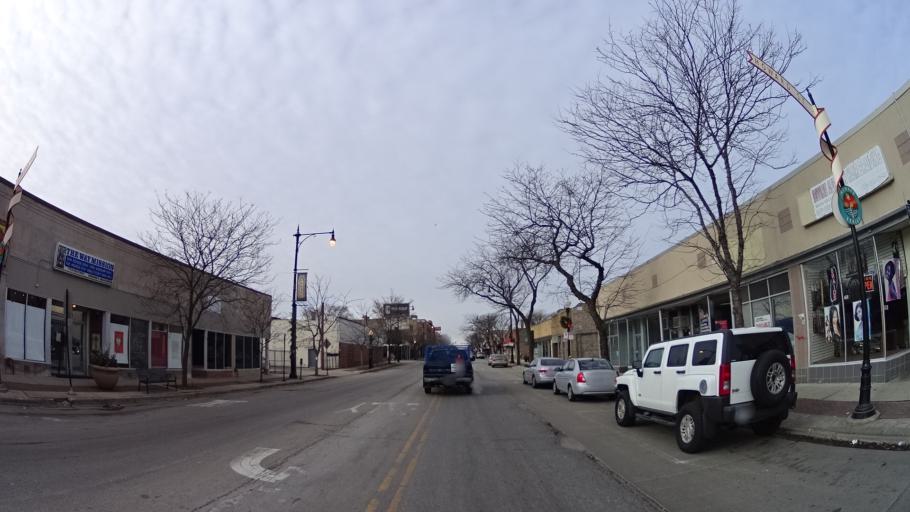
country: US
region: Illinois
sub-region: Cook County
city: Evanston
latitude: 42.0195
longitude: -87.6806
